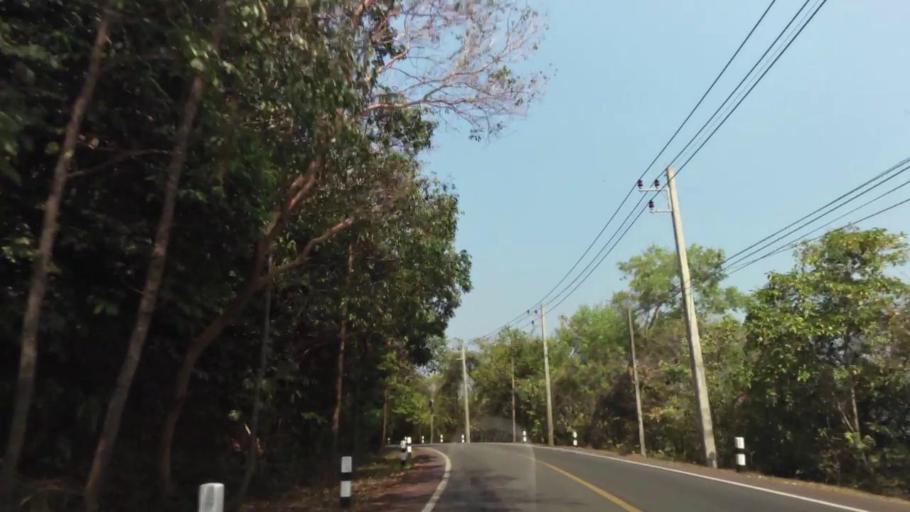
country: TH
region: Chanthaburi
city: Tha Mai
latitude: 12.5350
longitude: 101.9474
